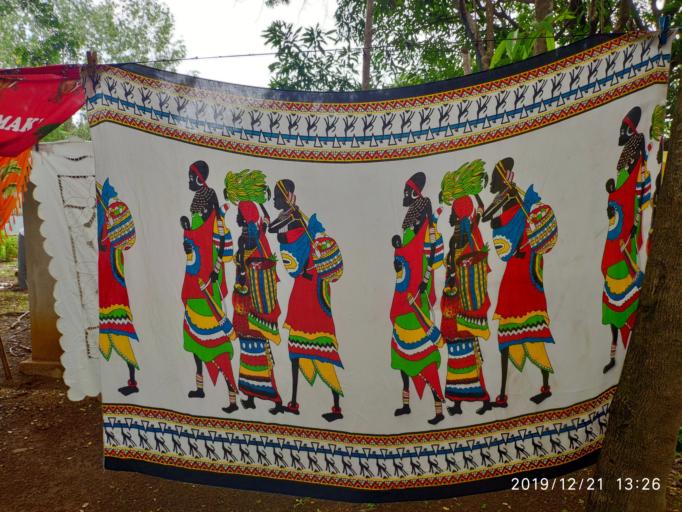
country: MG
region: Diana
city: Ambilobe
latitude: -12.9680
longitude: 49.1384
